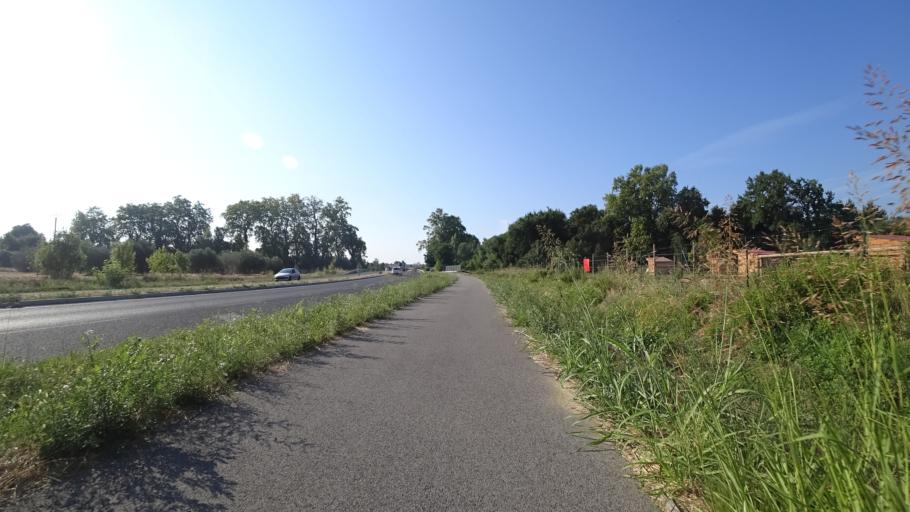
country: FR
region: Languedoc-Roussillon
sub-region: Departement des Pyrenees-Orientales
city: Perpignan
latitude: 42.7160
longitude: 2.9035
